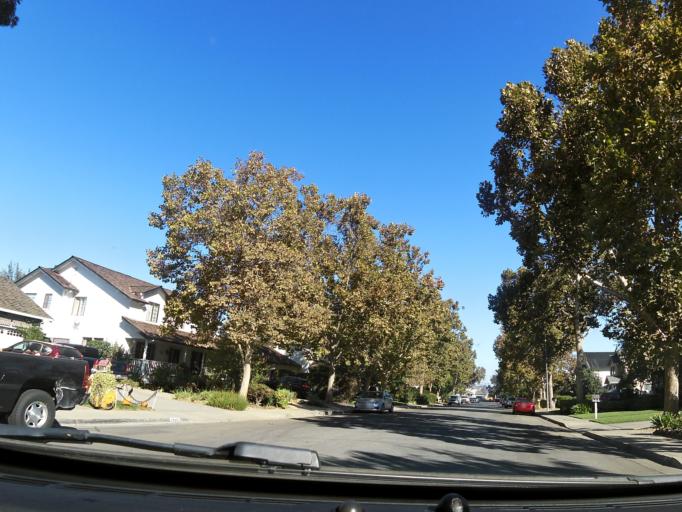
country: US
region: California
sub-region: San Benito County
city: Hollister
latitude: 36.8350
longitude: -121.3974
